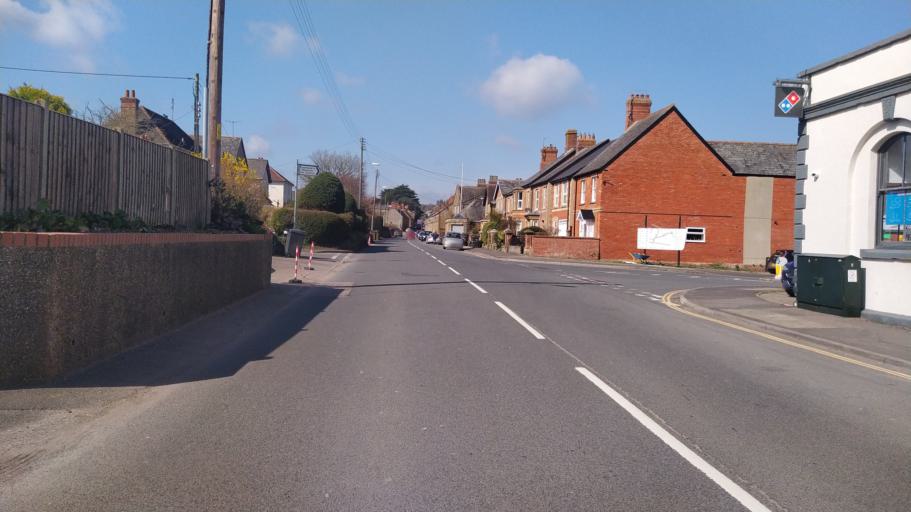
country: GB
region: England
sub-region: Somerset
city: Crewkerne
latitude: 50.8810
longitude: -2.7888
